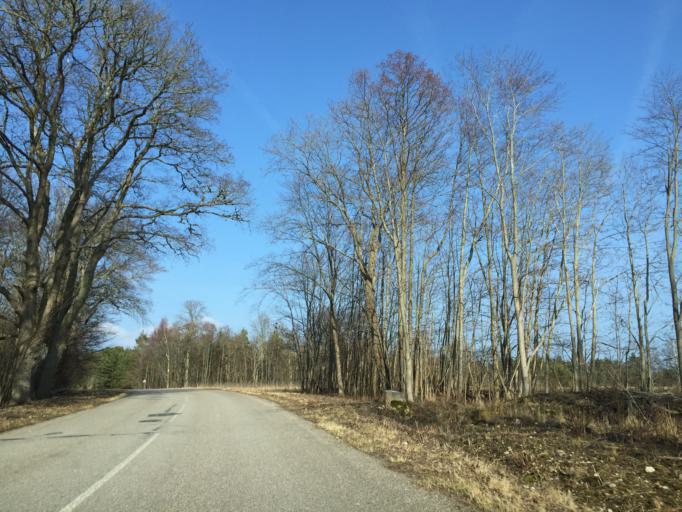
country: EE
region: Saare
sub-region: Kuressaare linn
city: Kuressaare
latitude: 58.0180
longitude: 22.0788
